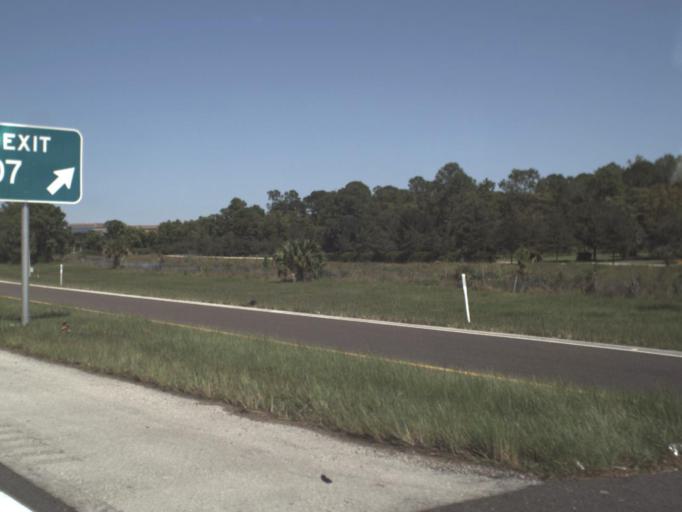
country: US
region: Florida
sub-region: Collier County
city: Vineyards
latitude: 26.2066
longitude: -81.7359
